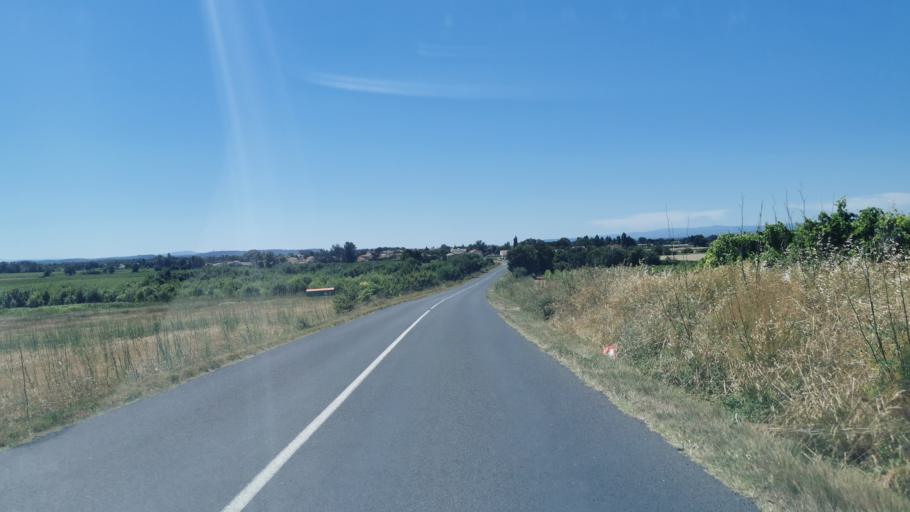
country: FR
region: Languedoc-Roussillon
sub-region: Departement de l'Aude
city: Coursan
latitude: 43.2327
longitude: 3.0822
